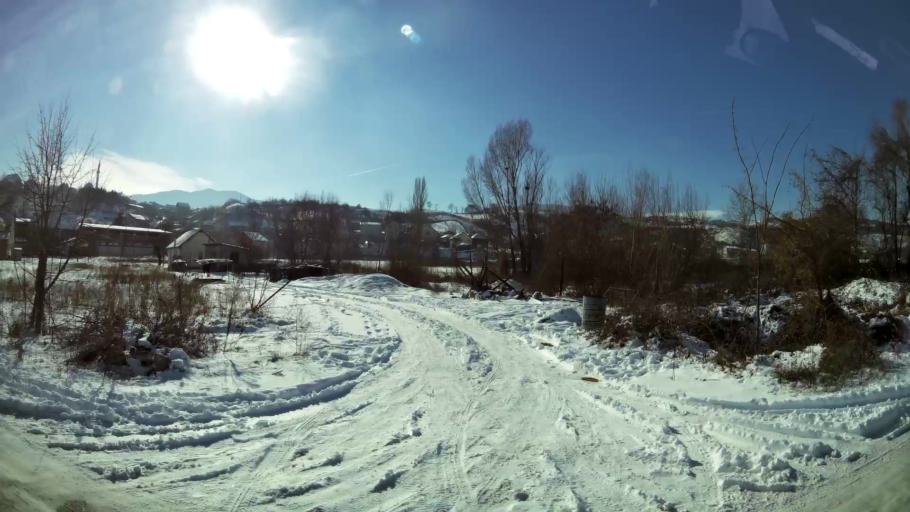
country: MK
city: Ljubin
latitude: 42.0049
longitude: 21.3057
